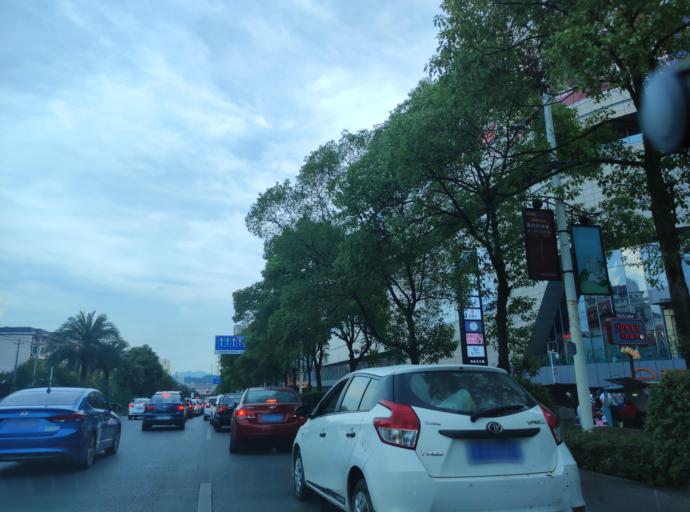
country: CN
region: Jiangxi Sheng
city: Pingxiang
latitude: 27.6354
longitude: 113.8695
